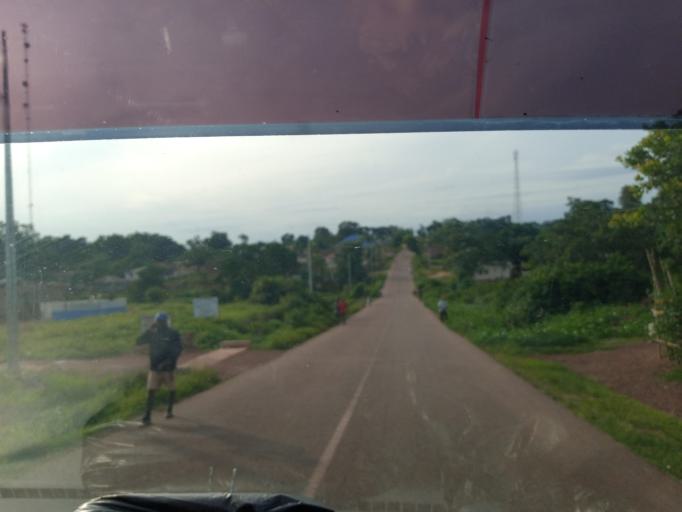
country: SL
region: Southern Province
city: Largo
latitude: 8.1973
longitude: -12.0585
